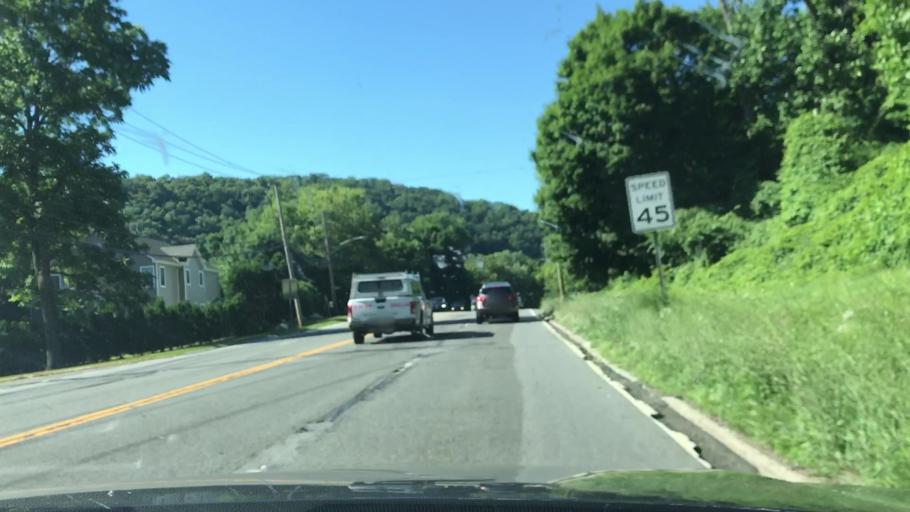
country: US
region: New York
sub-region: Westchester County
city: Hawthorne
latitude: 41.1027
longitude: -73.8079
